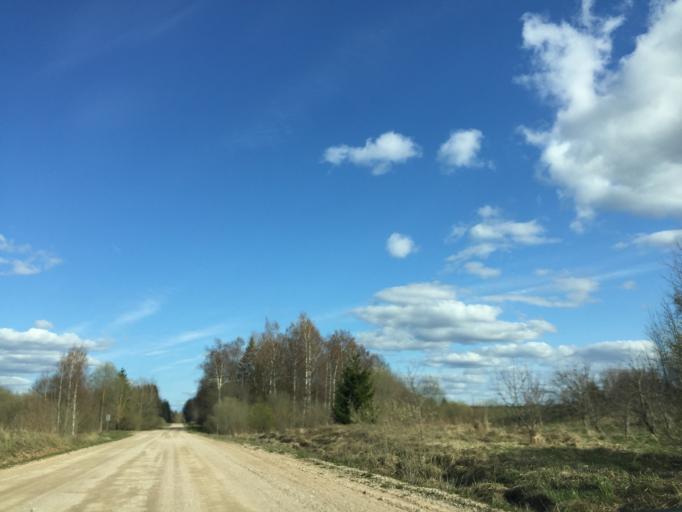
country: LV
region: Rezekne
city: Rezekne
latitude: 56.6474
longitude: 27.3671
